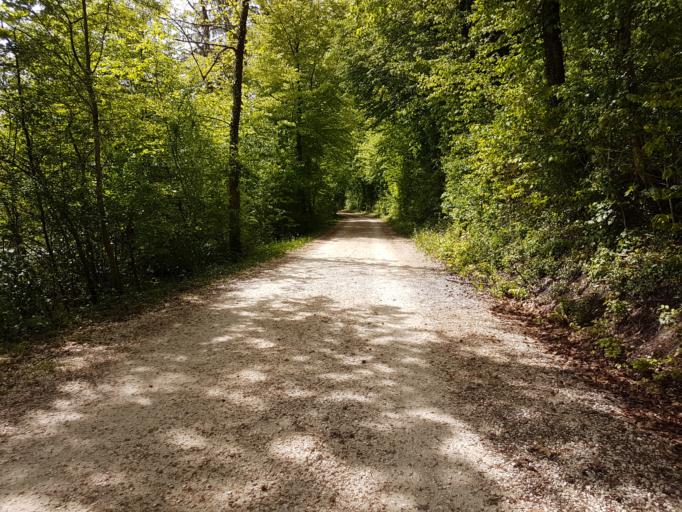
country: CH
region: Aargau
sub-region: Bezirk Brugg
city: Rupperswil
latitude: 47.4126
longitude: 8.1122
